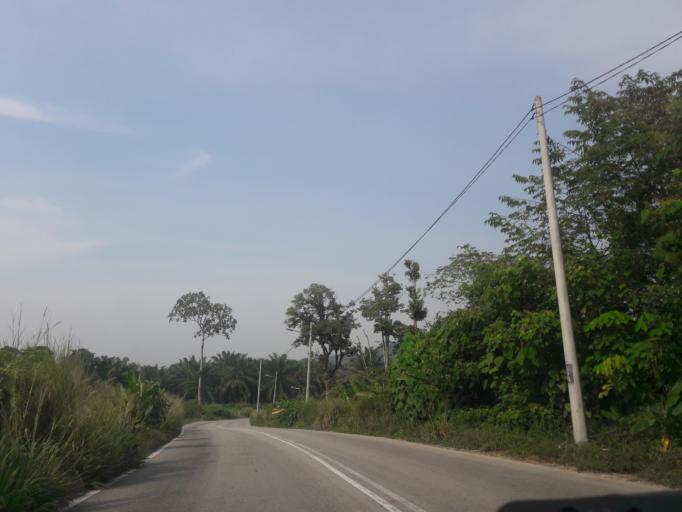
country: MY
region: Kedah
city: Kulim
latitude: 5.3635
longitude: 100.5223
